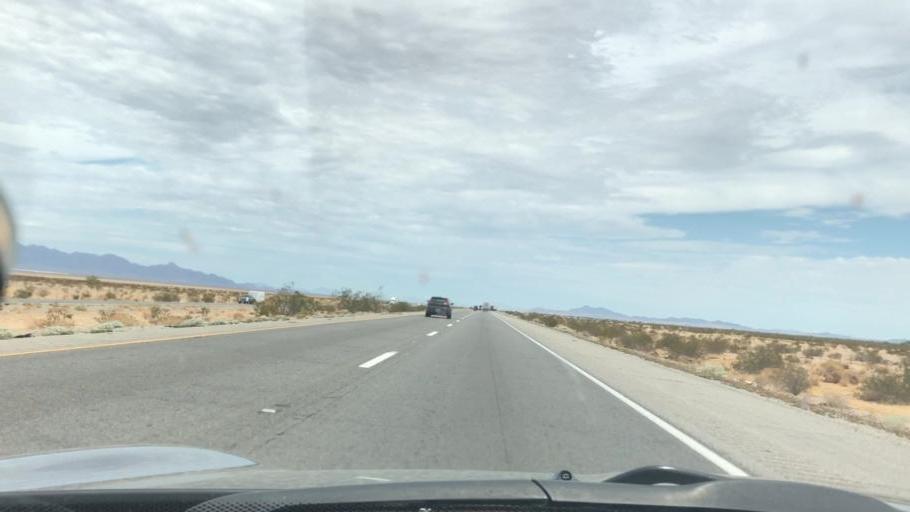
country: US
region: California
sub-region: Riverside County
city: Mesa Verde
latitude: 33.6377
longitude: -115.0892
